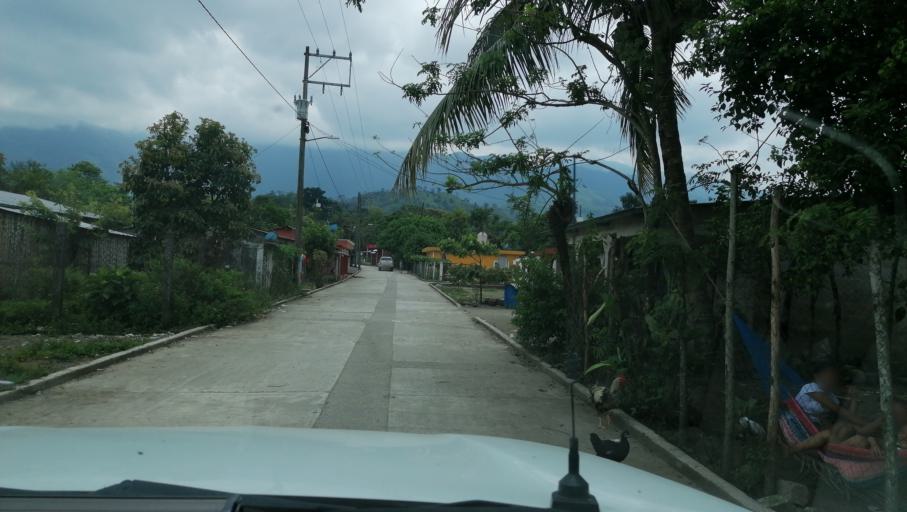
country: MX
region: Chiapas
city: Ocotepec
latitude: 17.2881
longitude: -93.2212
